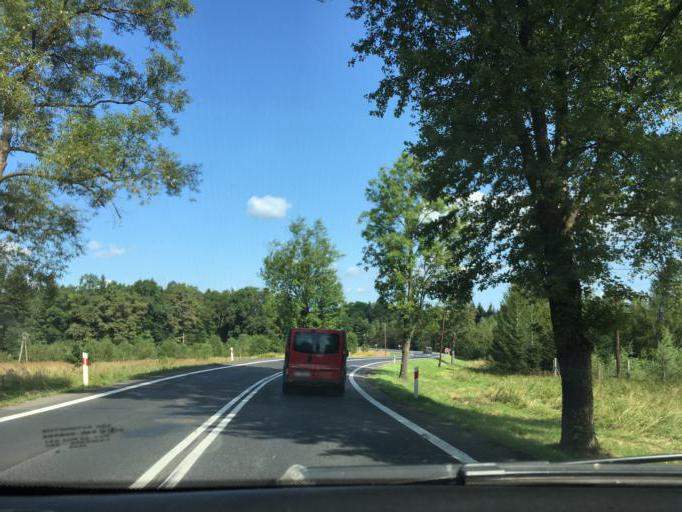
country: PL
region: Subcarpathian Voivodeship
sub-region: Powiat sanocki
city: Zagorz
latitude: 49.5071
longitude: 22.2941
